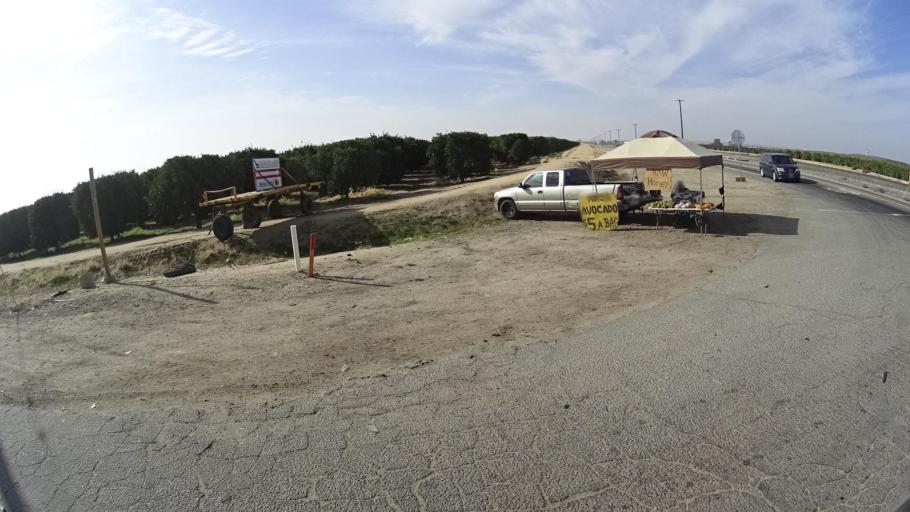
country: US
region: California
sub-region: Kern County
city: Lamont
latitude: 35.3411
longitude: -118.8432
